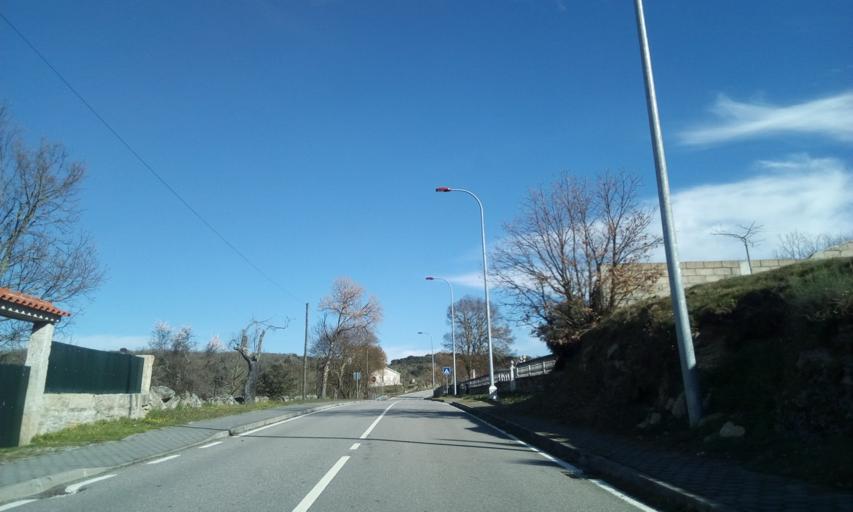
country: ES
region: Castille and Leon
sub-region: Provincia de Salamanca
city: Fuentes de Onoro
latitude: 40.6192
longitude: -6.8962
